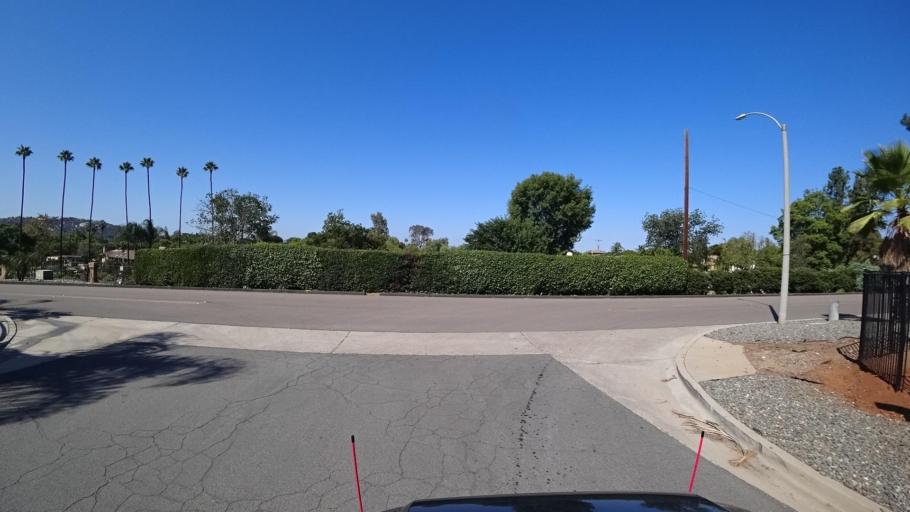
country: US
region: California
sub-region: San Diego County
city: Granite Hills
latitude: 32.7907
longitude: -116.8972
